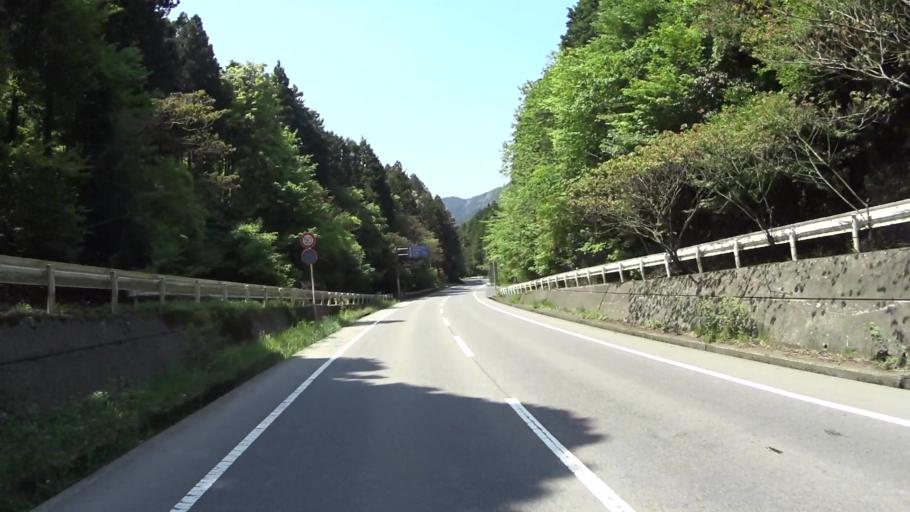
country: JP
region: Shiga Prefecture
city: Kitahama
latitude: 35.1591
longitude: 135.8520
